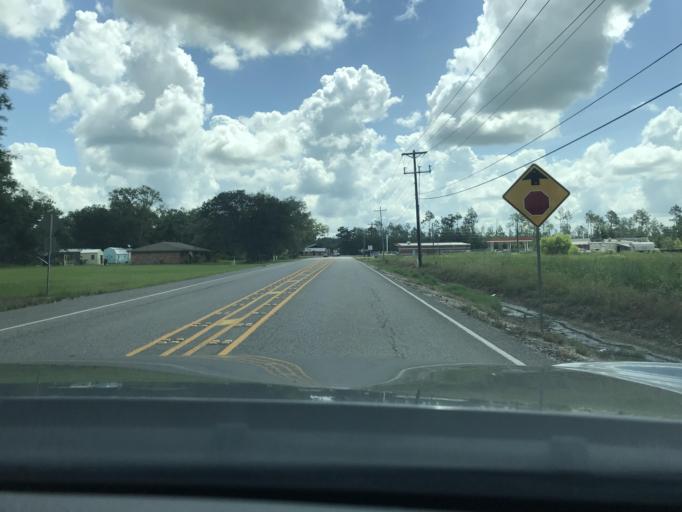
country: US
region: Louisiana
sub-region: Calcasieu Parish
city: Moss Bluff
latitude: 30.3445
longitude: -93.2030
